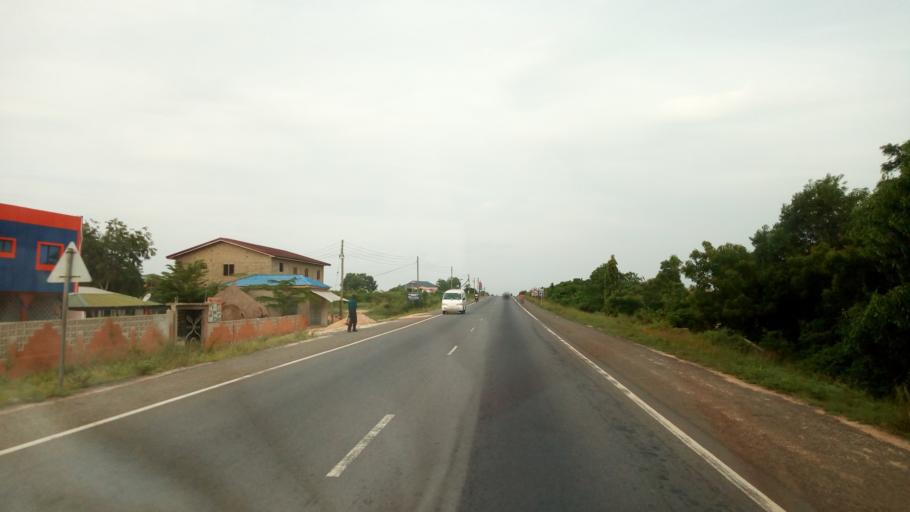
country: GH
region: Volta
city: Keta
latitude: 6.0579
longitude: 0.9903
